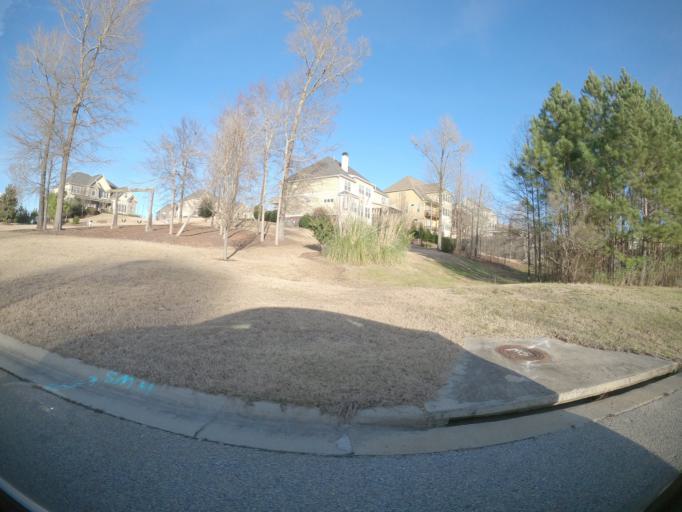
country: US
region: Georgia
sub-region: Columbia County
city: Evans
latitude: 33.5898
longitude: -82.2014
